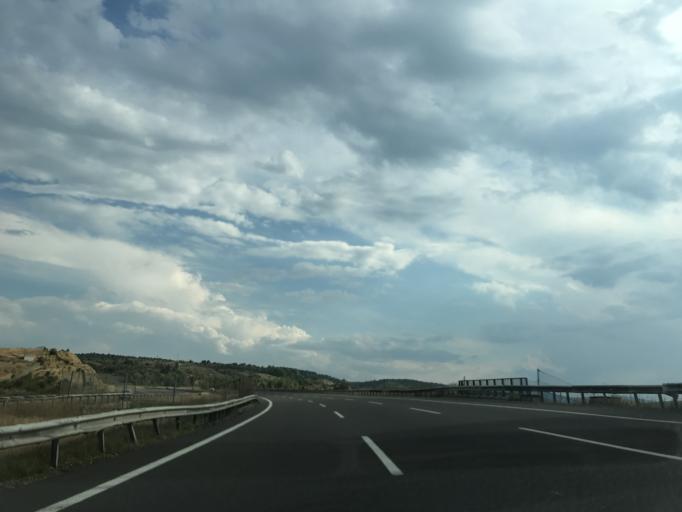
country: TR
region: Bolu
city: Gerede
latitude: 40.6591
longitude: 32.2366
